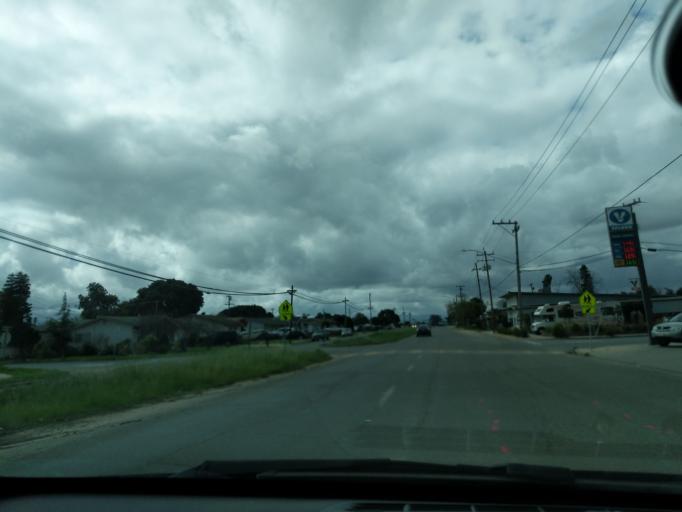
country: US
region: California
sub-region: Monterey County
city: Boronda
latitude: 36.7338
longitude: -121.6381
